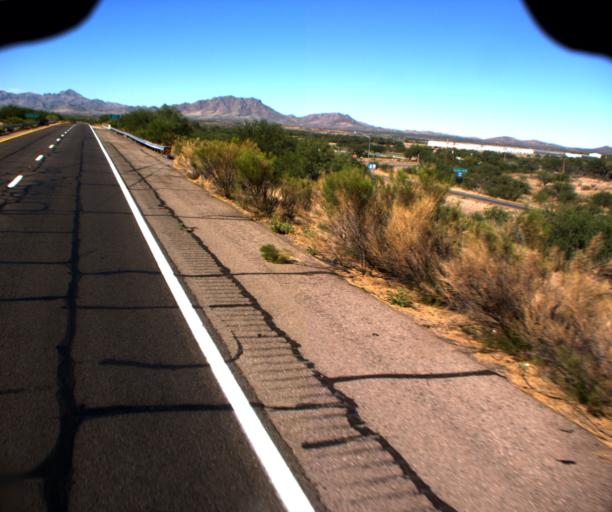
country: US
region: Arizona
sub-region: Pima County
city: Arivaca Junction
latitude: 31.7275
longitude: -111.0578
